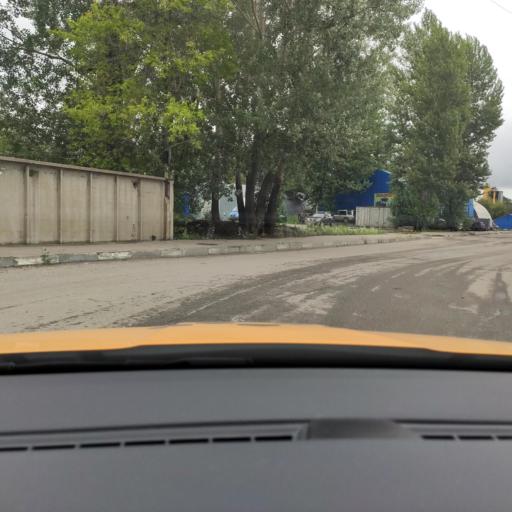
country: RU
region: Moskovskaya
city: Kozhukhovo
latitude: 55.6998
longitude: 37.7002
